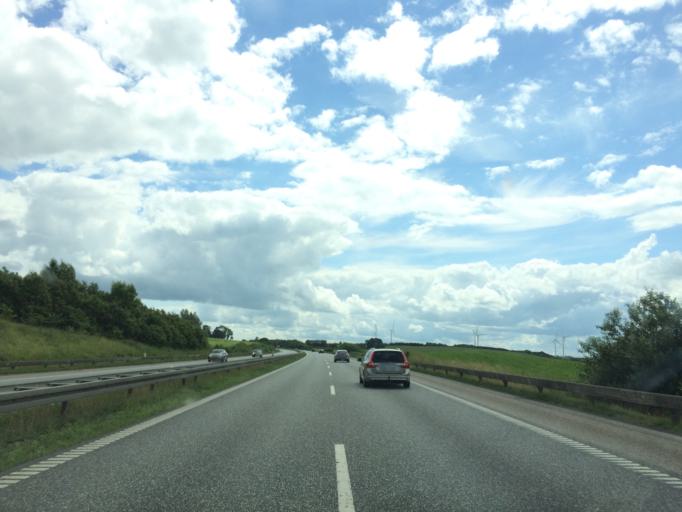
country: DK
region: North Denmark
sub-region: Mariagerfjord Kommune
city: Hobro
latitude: 56.6955
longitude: 9.7288
